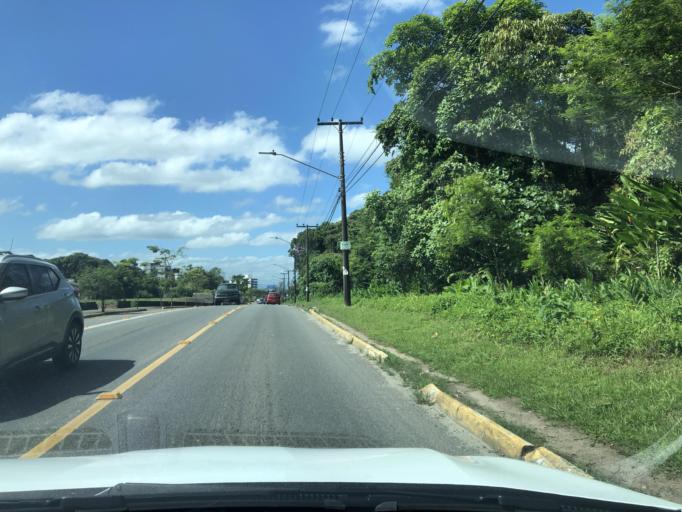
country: BR
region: Santa Catarina
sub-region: Joinville
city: Joinville
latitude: -26.2781
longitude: -48.8636
